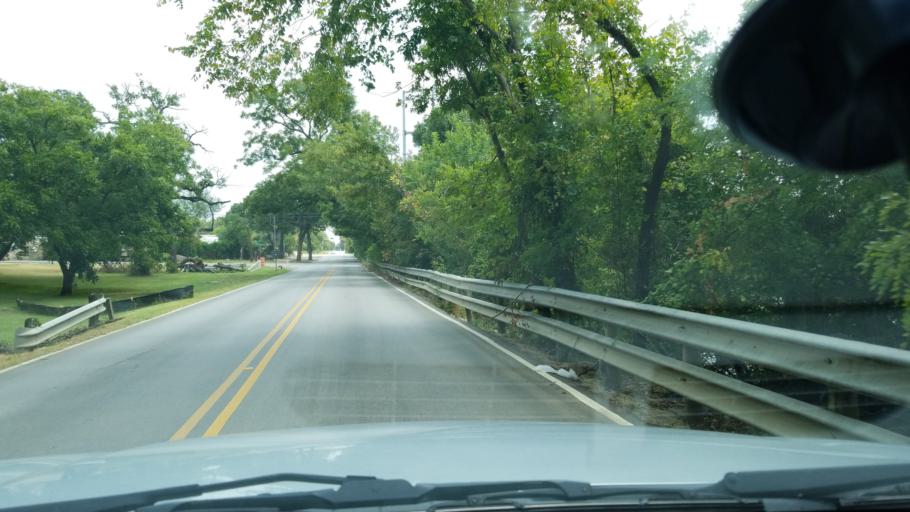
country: US
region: Texas
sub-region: Dallas County
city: Irving
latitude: 32.8668
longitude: -96.9209
